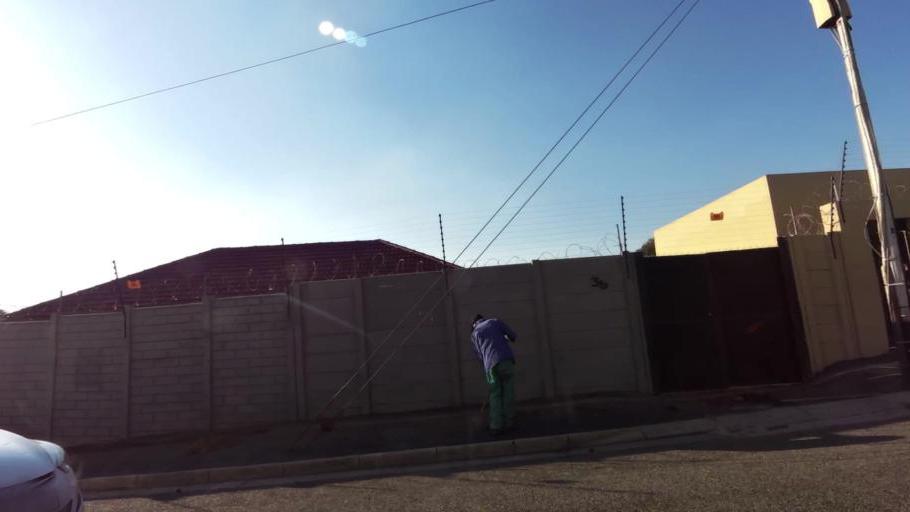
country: ZA
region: Gauteng
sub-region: City of Johannesburg Metropolitan Municipality
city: Johannesburg
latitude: -26.1901
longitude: 27.9971
